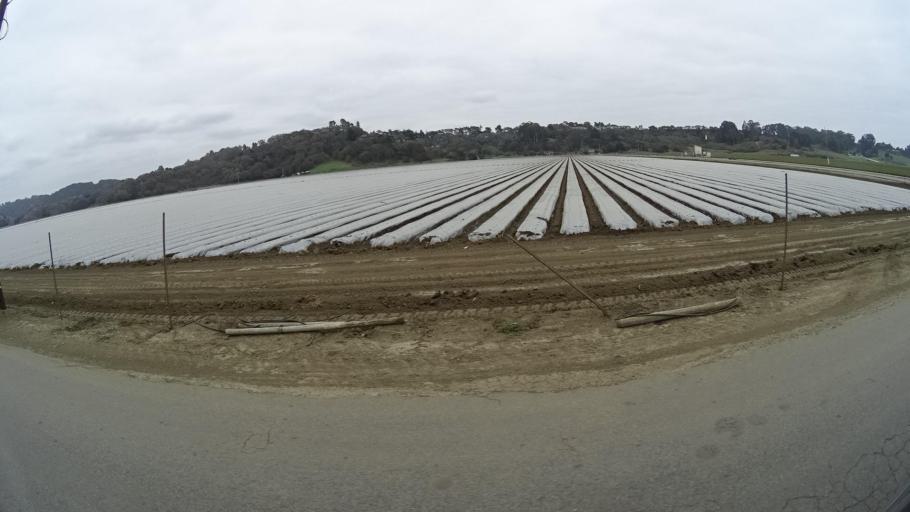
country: US
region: California
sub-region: Monterey County
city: Pajaro
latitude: 36.8847
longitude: -121.7595
